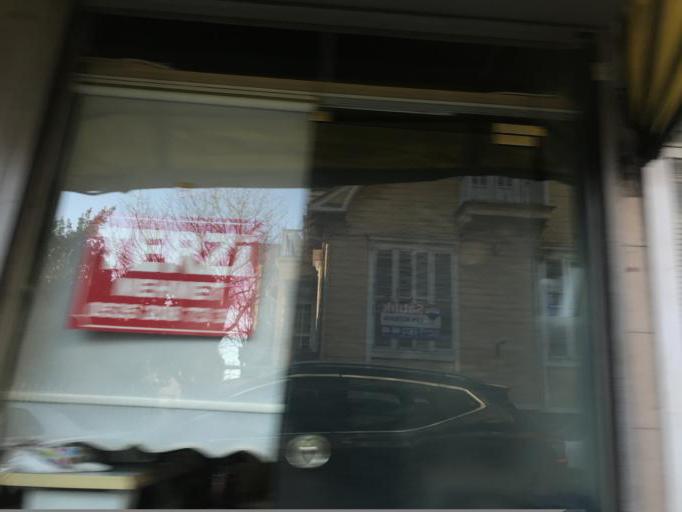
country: TR
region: Istanbul
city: Bahcelievler
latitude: 40.9623
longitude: 28.8240
